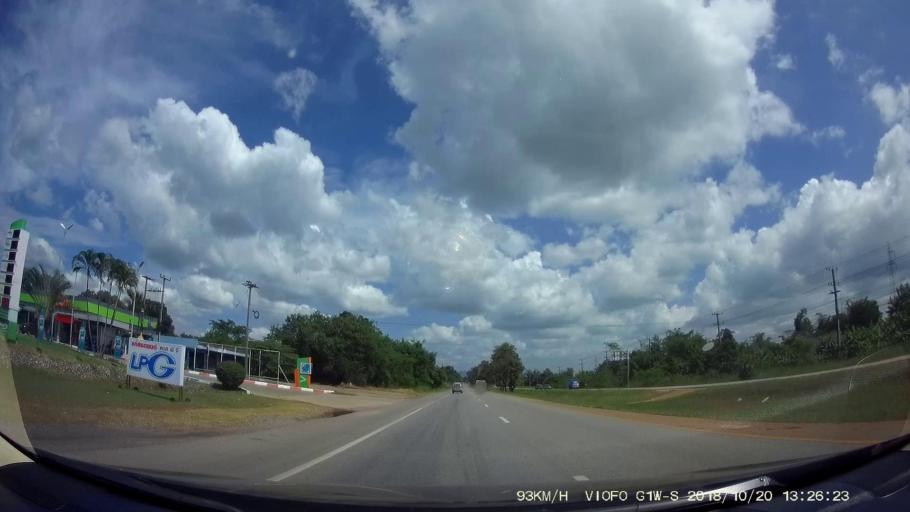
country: TH
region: Chaiyaphum
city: Khon San
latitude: 16.5939
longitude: 101.9454
